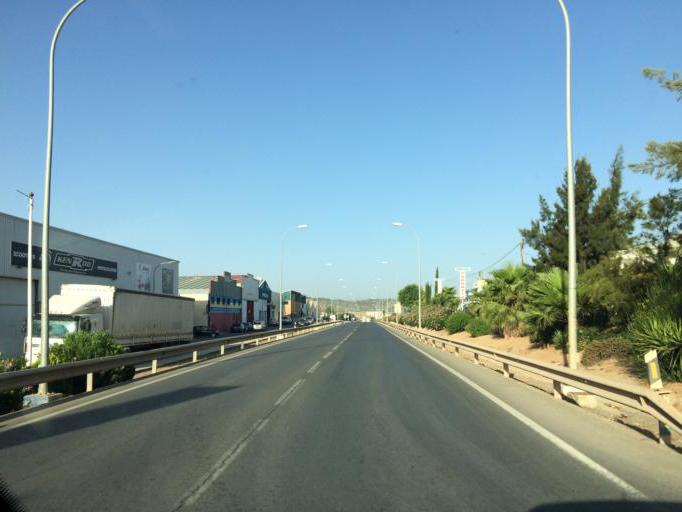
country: ES
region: Andalusia
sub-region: Provincia de Malaga
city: Campillos
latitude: 37.0508
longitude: -4.8724
